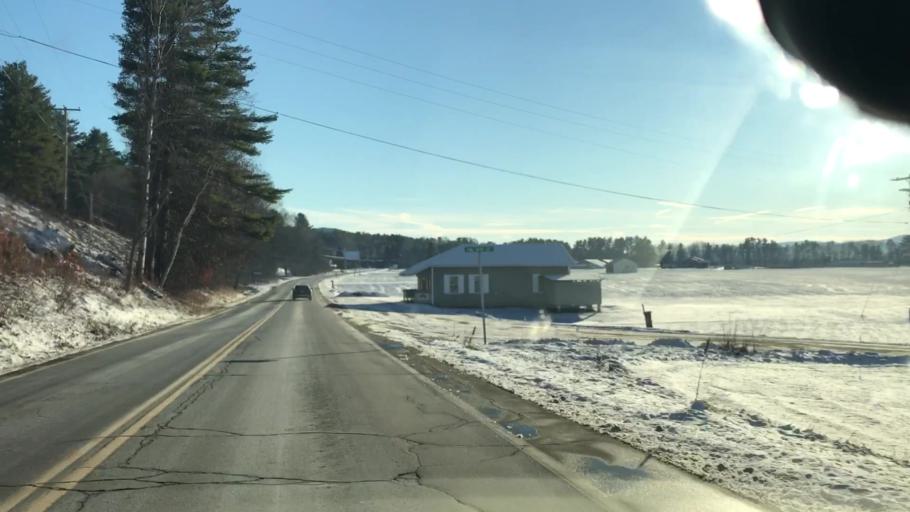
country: US
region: New Hampshire
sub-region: Grafton County
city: Haverhill
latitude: 44.0632
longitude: -72.0485
